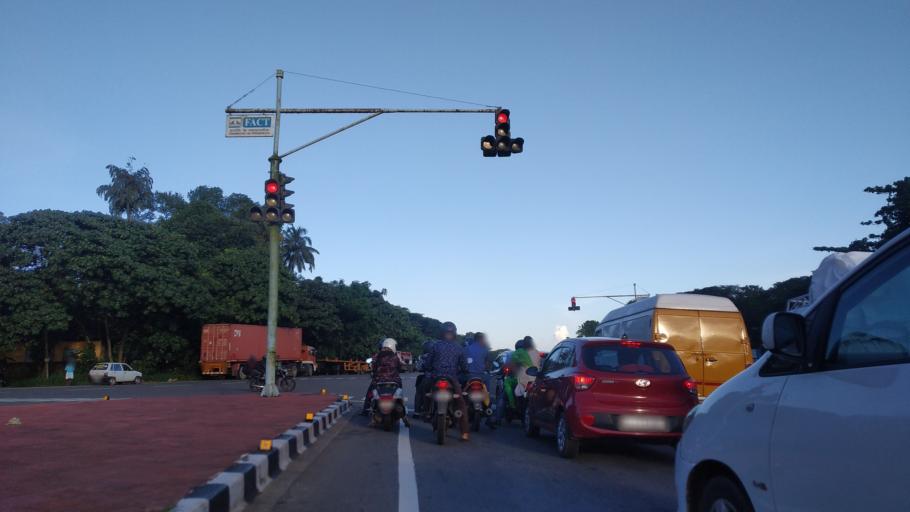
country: IN
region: Kerala
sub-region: Ernakulam
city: Elur
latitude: 10.0698
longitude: 76.3050
